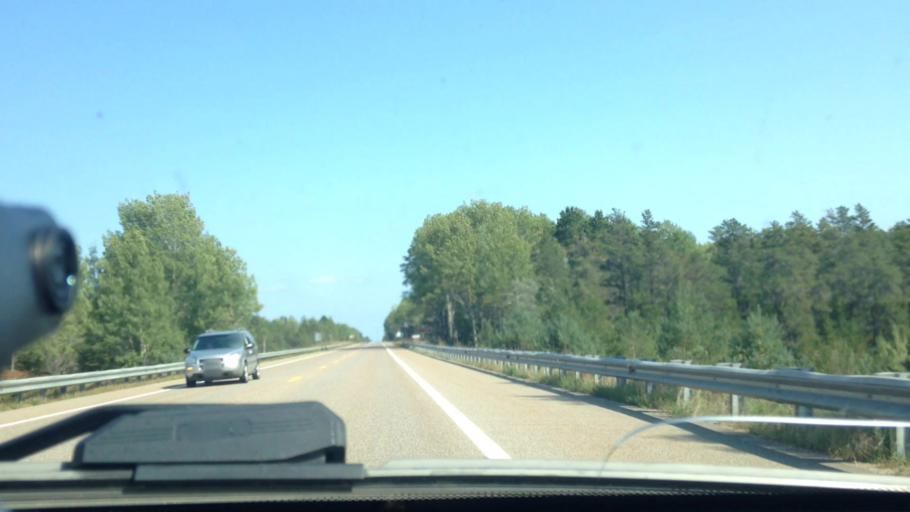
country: US
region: Michigan
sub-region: Mackinac County
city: Saint Ignace
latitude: 46.3584
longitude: -84.8670
